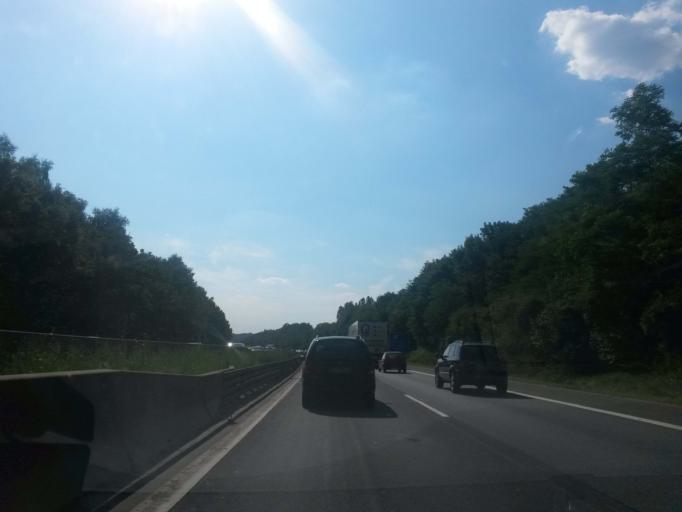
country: DE
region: Bavaria
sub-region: Regierungsbezirk Mittelfranken
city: Wendelstein
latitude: 49.3950
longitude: 11.1067
